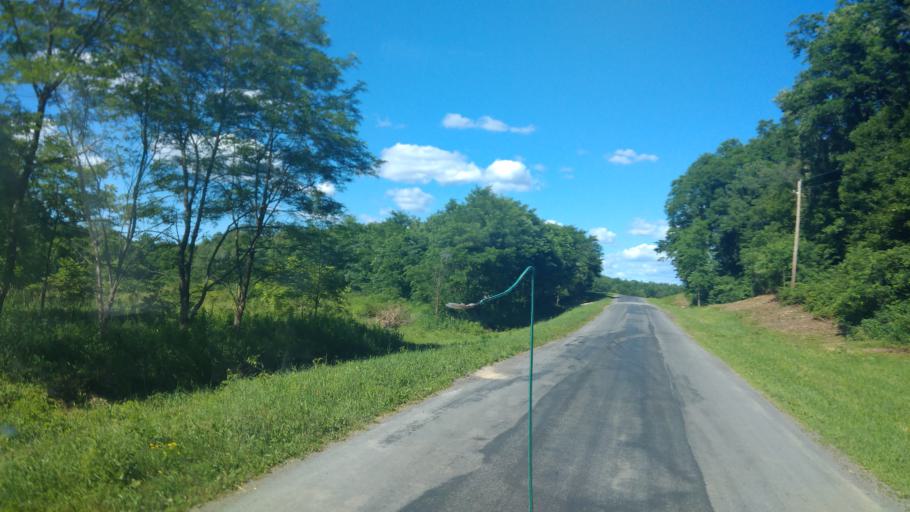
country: US
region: New York
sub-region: Wayne County
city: Clyde
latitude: 43.0246
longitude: -76.8446
